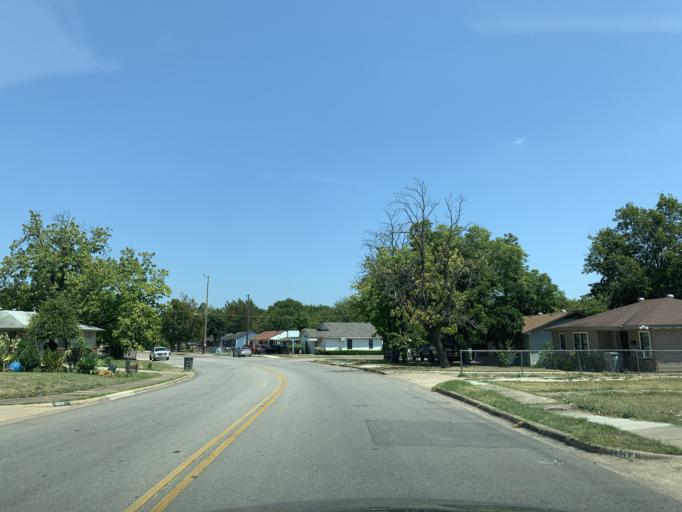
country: US
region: Texas
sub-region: Dallas County
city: Dallas
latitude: 32.6924
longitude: -96.8051
